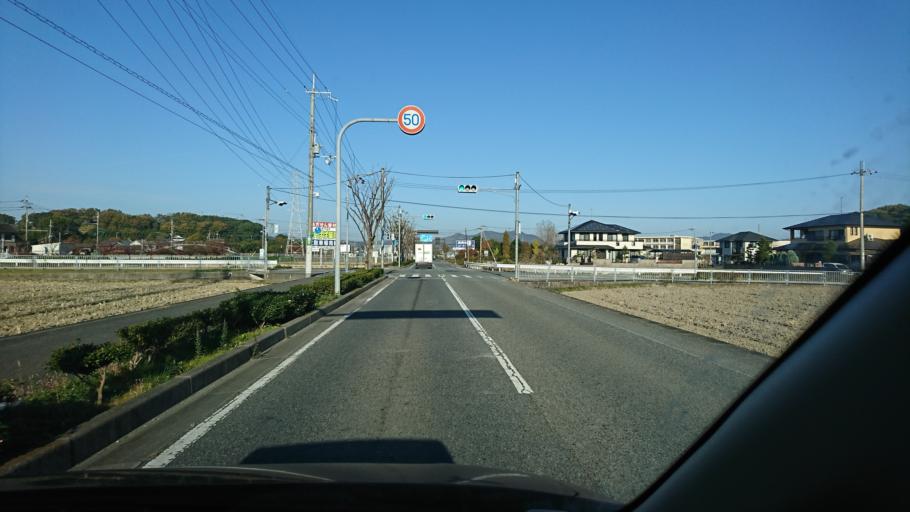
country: JP
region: Hyogo
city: Kakogawacho-honmachi
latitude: 34.7732
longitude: 134.8789
